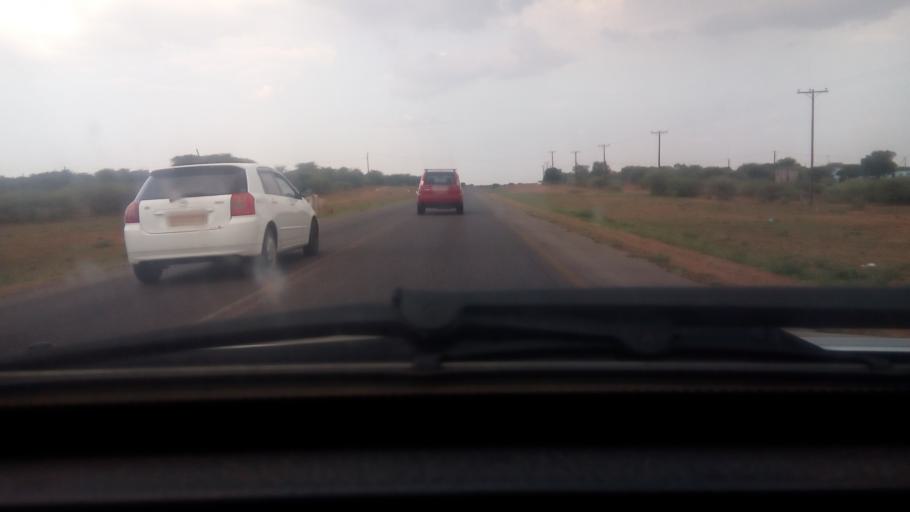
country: BW
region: Kweneng
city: Metsemotlhaba
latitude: -24.4649
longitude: 25.6671
